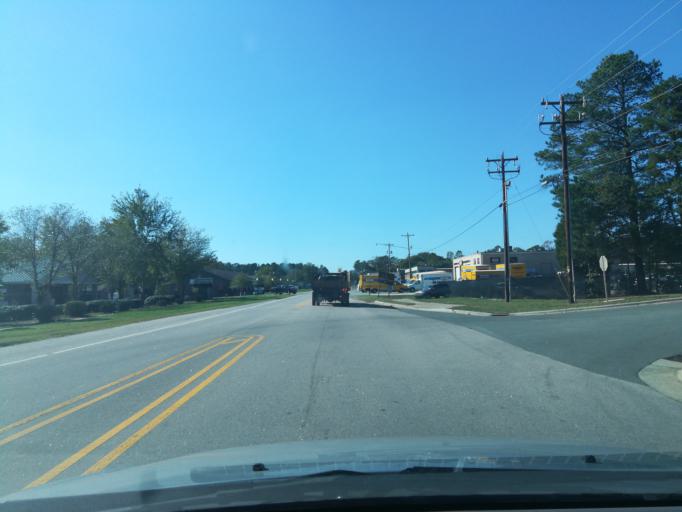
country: US
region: North Carolina
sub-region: Durham County
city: Durham
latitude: 36.0336
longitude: -78.9725
